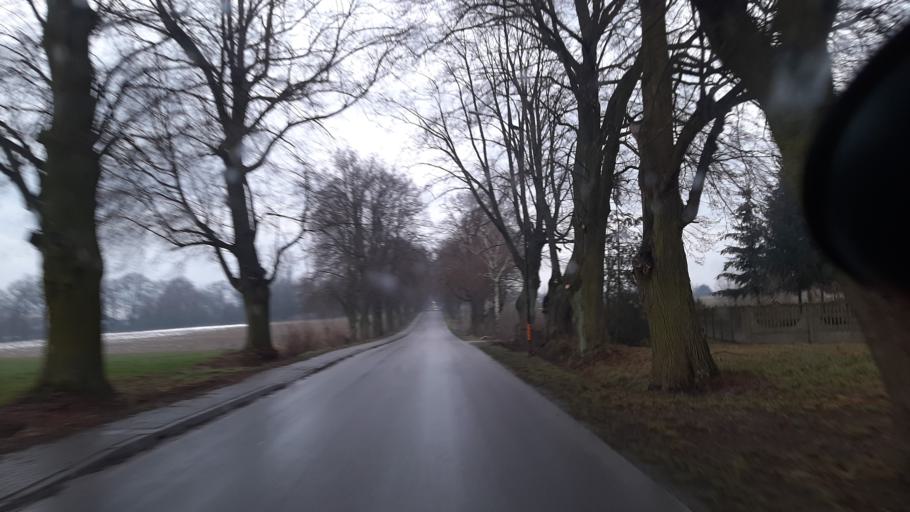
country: PL
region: Lublin Voivodeship
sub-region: Powiat lubelski
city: Lublin
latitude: 51.3300
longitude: 22.5565
